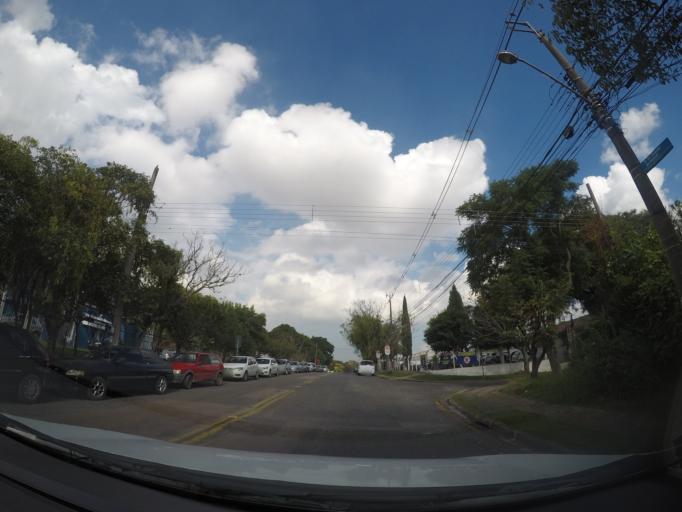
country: BR
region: Parana
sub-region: Curitiba
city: Curitiba
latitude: -25.4545
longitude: -49.2393
